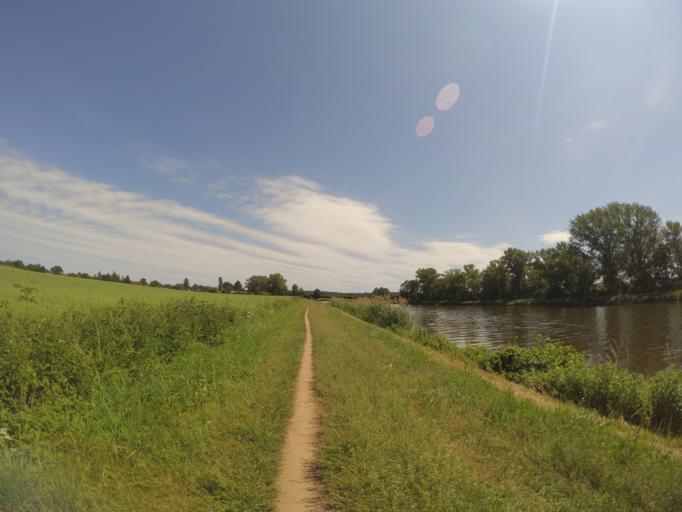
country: CZ
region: Central Bohemia
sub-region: Okres Nymburk
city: Sadska
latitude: 50.1658
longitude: 14.9564
